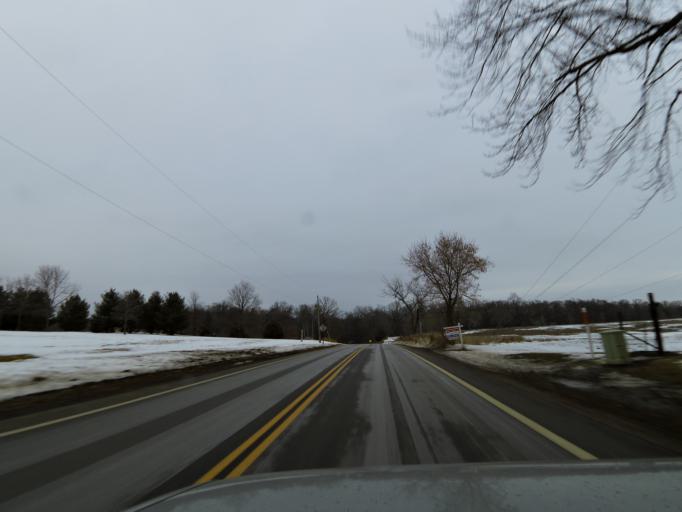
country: US
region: Minnesota
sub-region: Washington County
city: Afton
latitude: 44.8280
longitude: -92.7992
